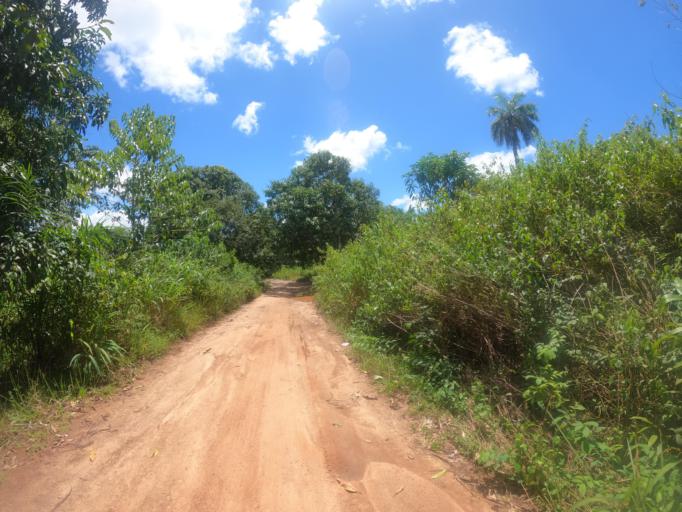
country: SL
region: Northern Province
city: Makeni
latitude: 8.8582
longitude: -12.1116
